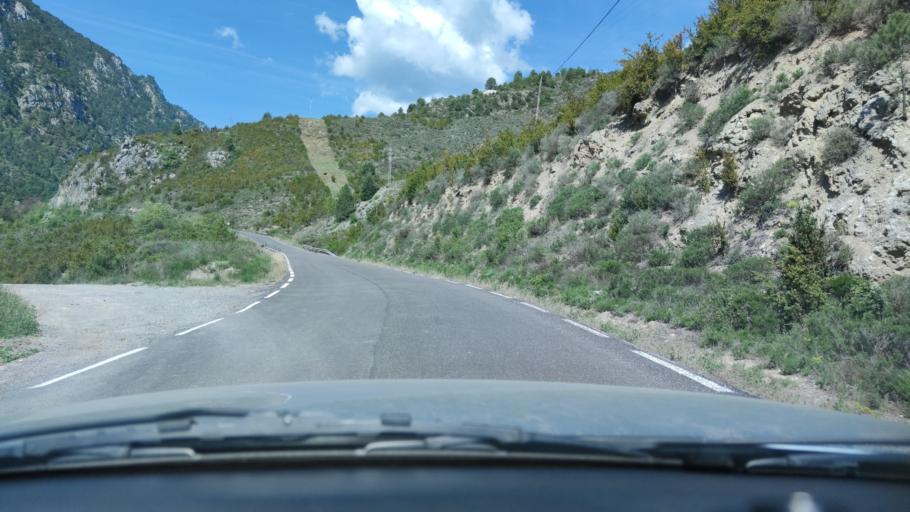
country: ES
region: Catalonia
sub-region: Provincia de Lleida
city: Coll de Nargo
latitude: 42.2922
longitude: 1.3284
